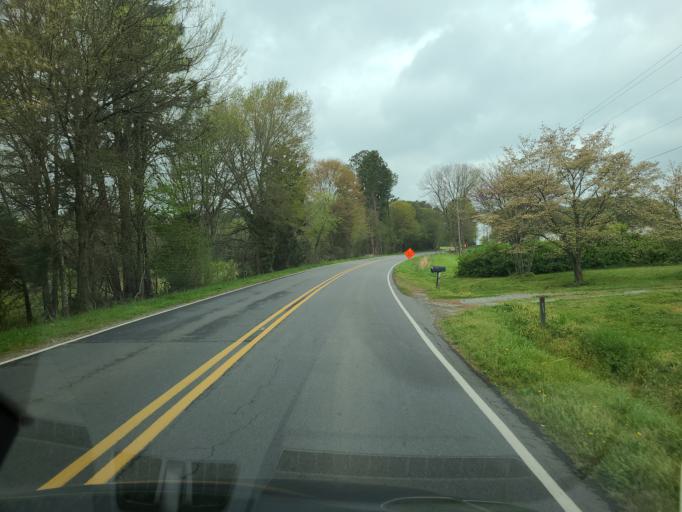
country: US
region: North Carolina
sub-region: Lincoln County
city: Lincolnton
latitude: 35.4616
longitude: -81.2826
